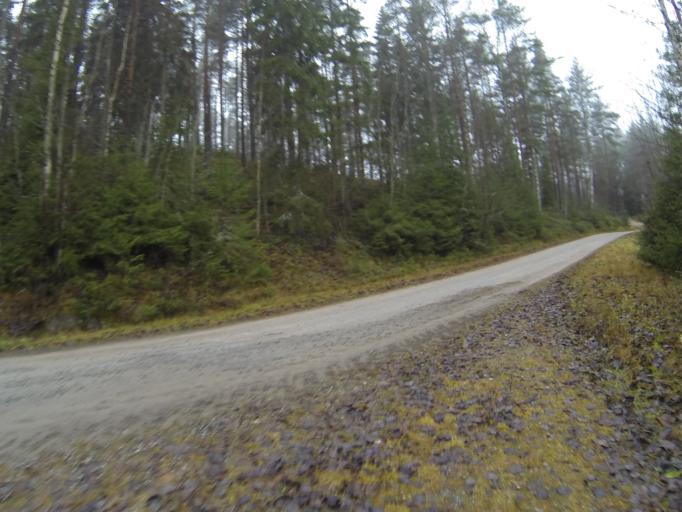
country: FI
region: Varsinais-Suomi
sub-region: Salo
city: Halikko
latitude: 60.4142
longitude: 22.9286
